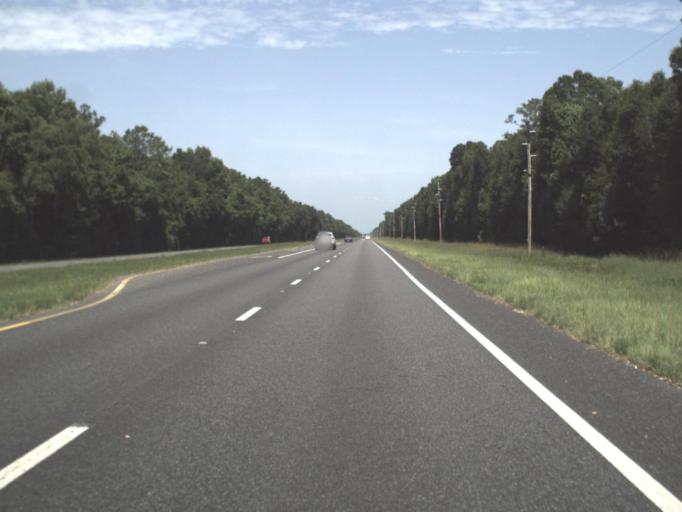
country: US
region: Florida
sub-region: Dixie County
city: Cross City
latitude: 29.6587
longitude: -83.1907
